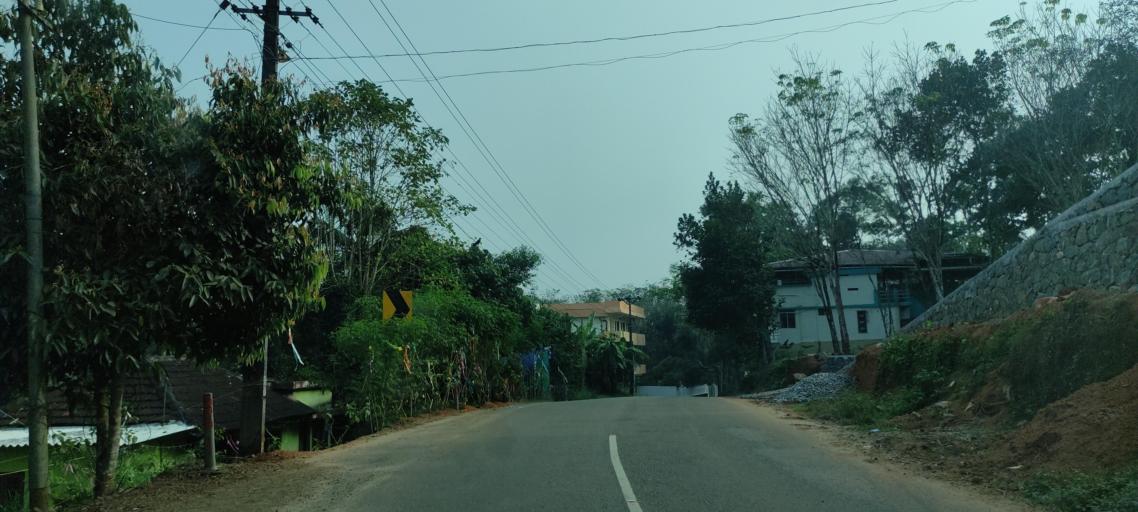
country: IN
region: Kerala
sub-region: Ernakulam
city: Piravam
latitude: 9.7993
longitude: 76.4986
